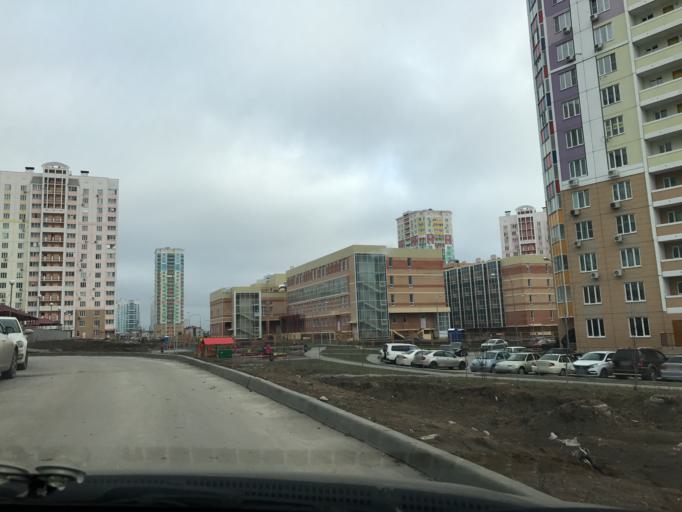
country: RU
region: Rostov
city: Kalinin
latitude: 47.2341
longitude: 39.5935
